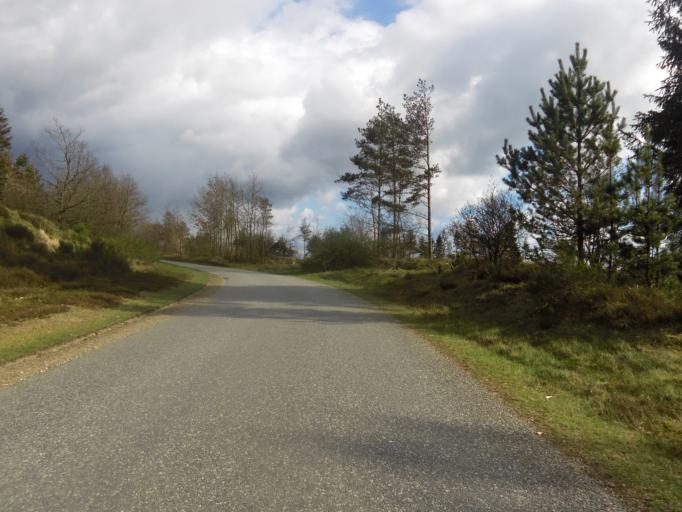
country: DK
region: South Denmark
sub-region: Haderslev Kommune
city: Gram
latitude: 55.2741
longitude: 8.9444
